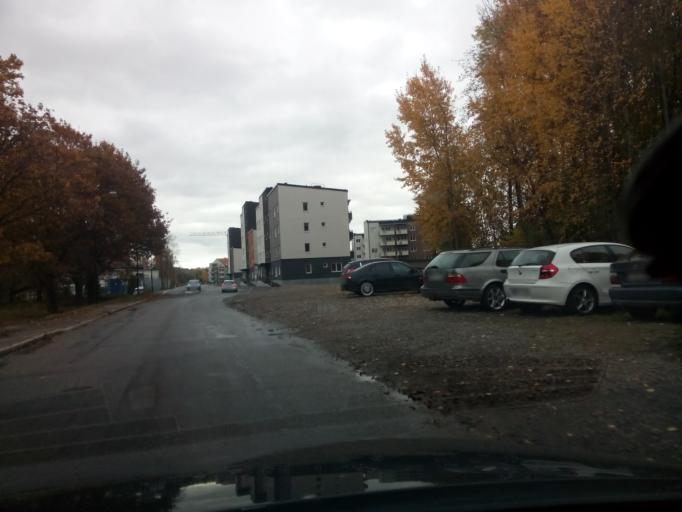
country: SE
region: Soedermanland
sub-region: Nykopings Kommun
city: Nykoping
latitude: 58.7491
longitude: 17.0222
